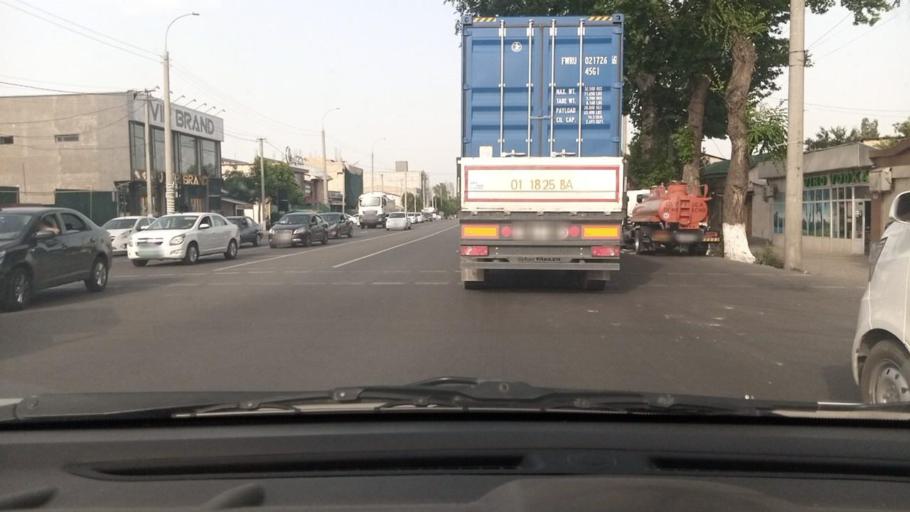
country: UZ
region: Toshkent
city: Salor
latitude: 41.3328
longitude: 69.2983
